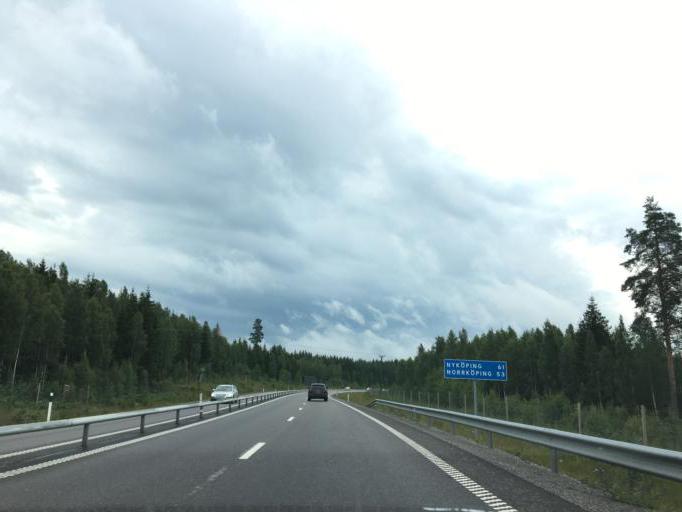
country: SE
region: Soedermanland
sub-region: Katrineholms Kommun
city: Katrineholm
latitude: 59.0067
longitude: 16.2402
